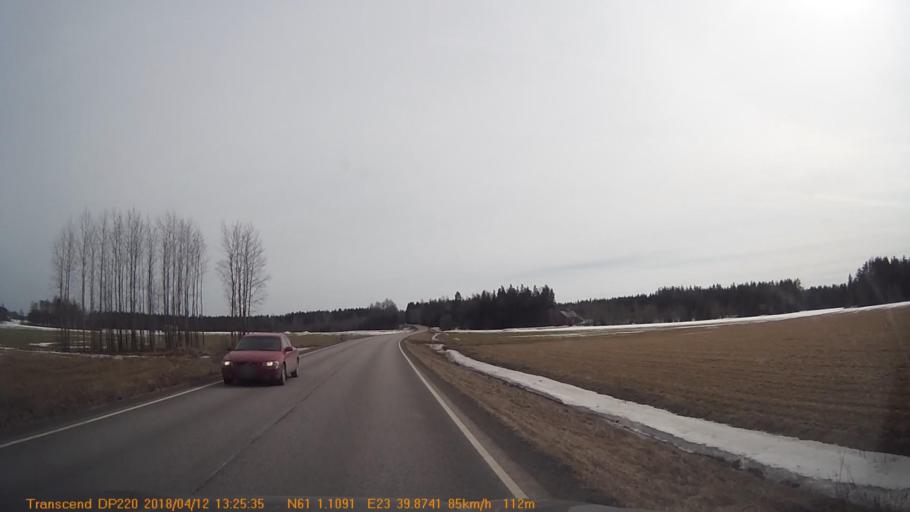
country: FI
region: Pirkanmaa
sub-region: Etelae-Pirkanmaa
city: Kylmaekoski
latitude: 61.0183
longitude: 23.6649
